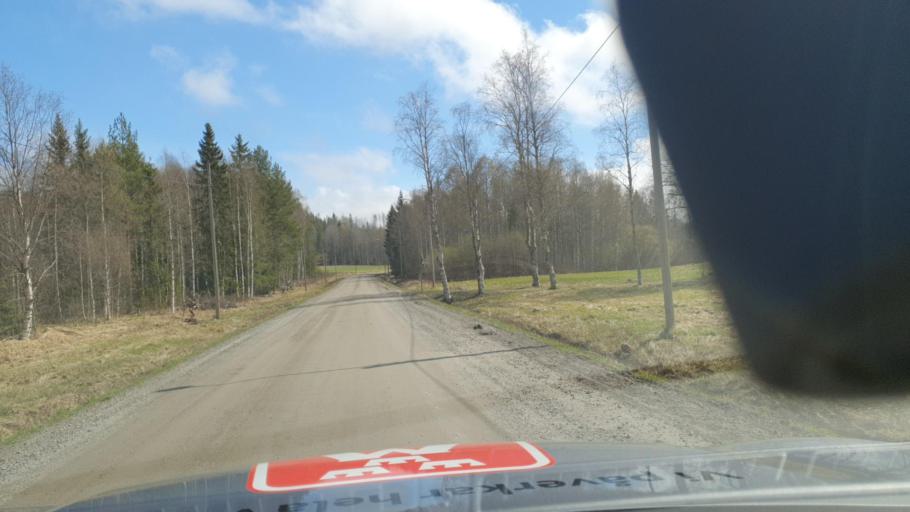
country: SE
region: Vaesterbotten
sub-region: Bjurholms Kommun
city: Bjurholm
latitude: 63.6959
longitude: 18.9534
